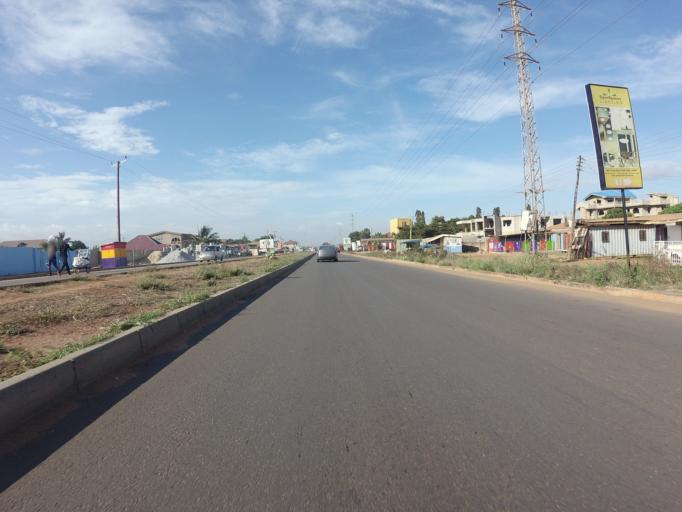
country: GH
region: Greater Accra
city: Nungua
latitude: 5.6341
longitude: -0.0644
